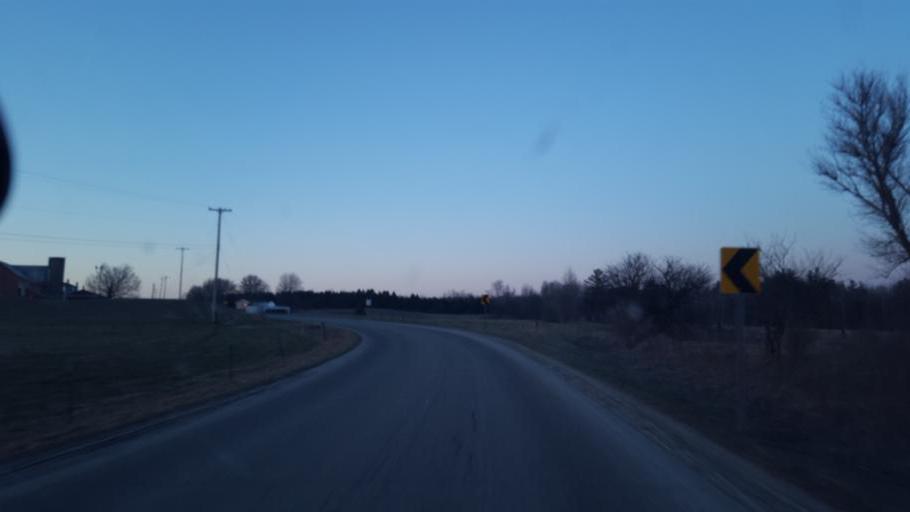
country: US
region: Michigan
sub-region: Montcalm County
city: Howard City
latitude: 43.5265
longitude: -85.4439
